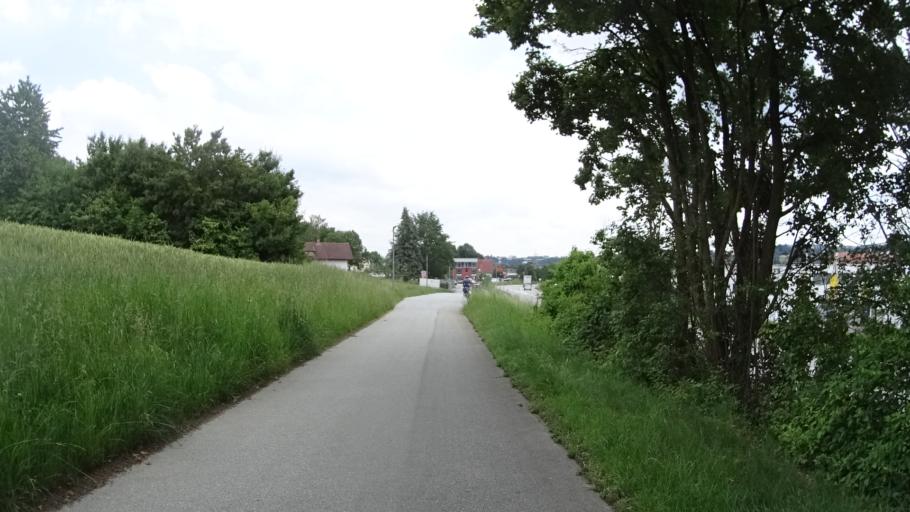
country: DE
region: Bavaria
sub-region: Lower Bavaria
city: Passau
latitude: 48.5837
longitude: 13.4080
